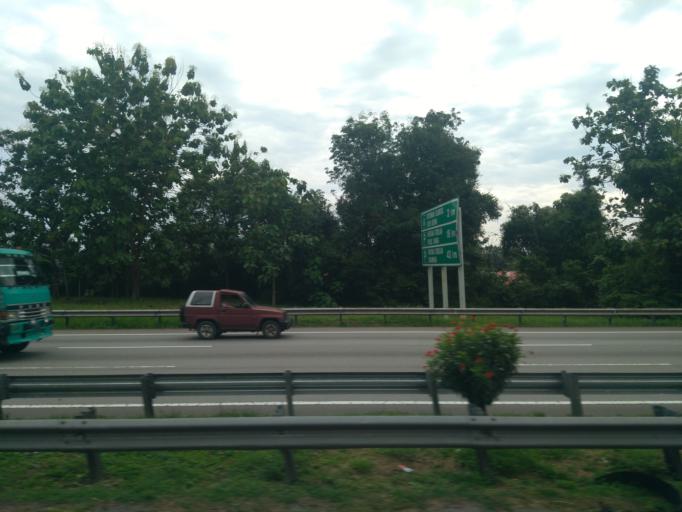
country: MY
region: Melaka
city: Alor Gajah
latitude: 2.3800
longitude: 102.2327
